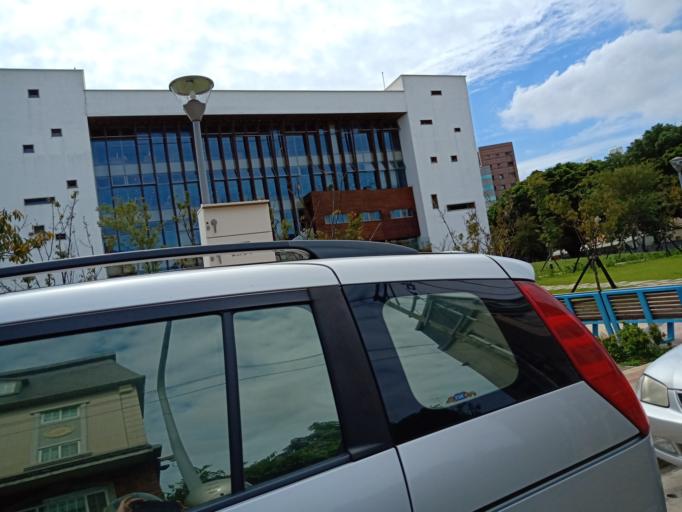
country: TW
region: Taiwan
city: Daxi
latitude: 24.9381
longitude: 121.2564
